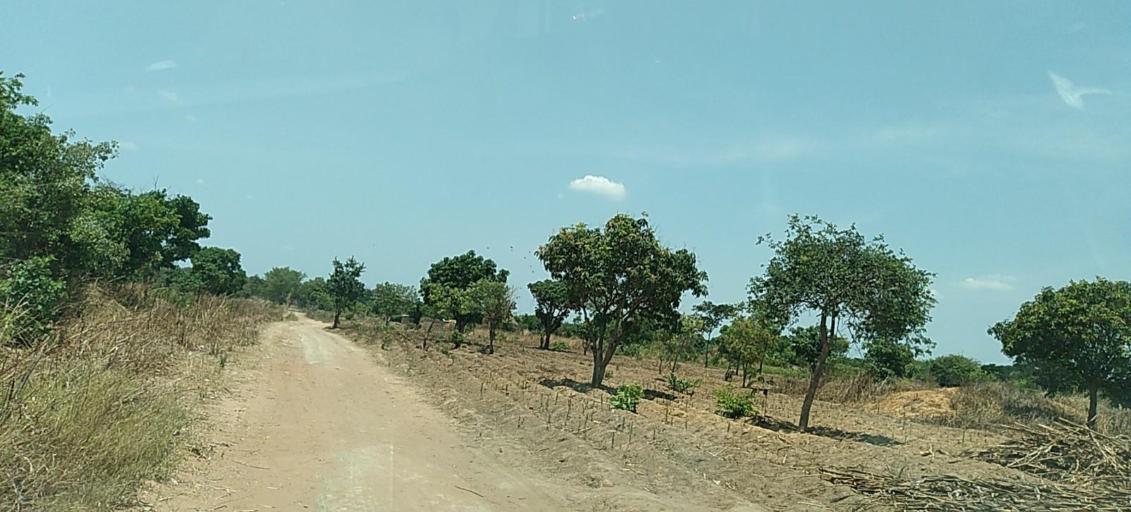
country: ZM
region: Copperbelt
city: Luanshya
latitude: -13.0714
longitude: 28.4064
